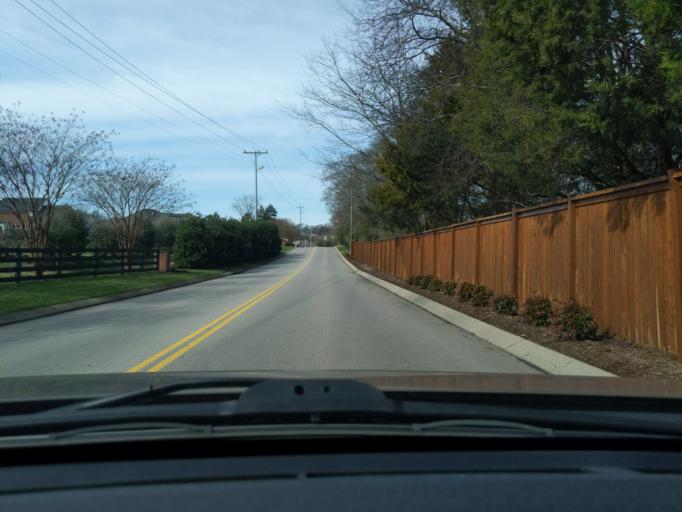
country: US
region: Tennessee
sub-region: Wilson County
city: Mount Juliet
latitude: 36.1670
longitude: -86.4883
